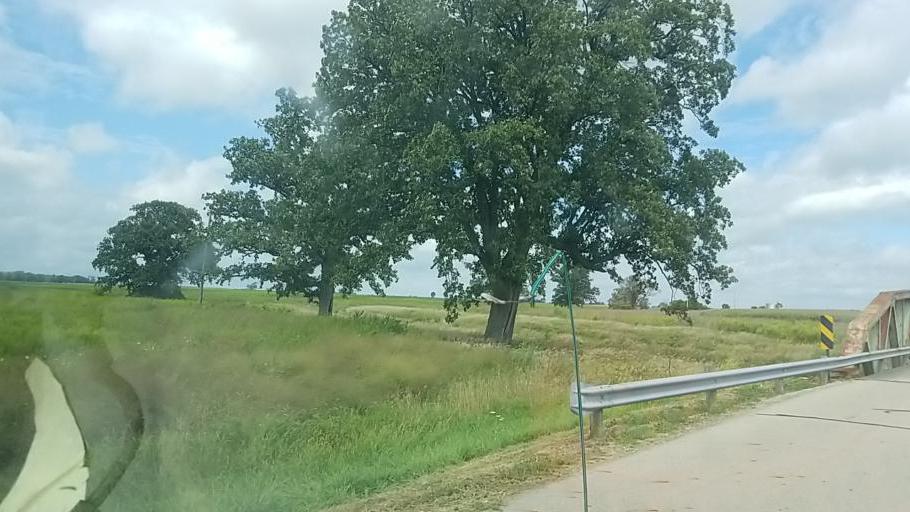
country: US
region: Ohio
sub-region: Fayette County
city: Jeffersonville
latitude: 39.6930
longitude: -83.5764
